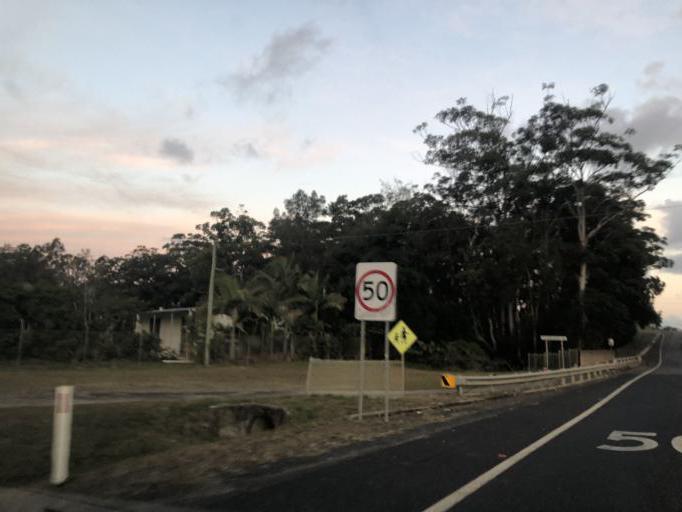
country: AU
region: New South Wales
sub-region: Coffs Harbour
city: Woolgoolga
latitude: -30.1056
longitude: 153.1884
